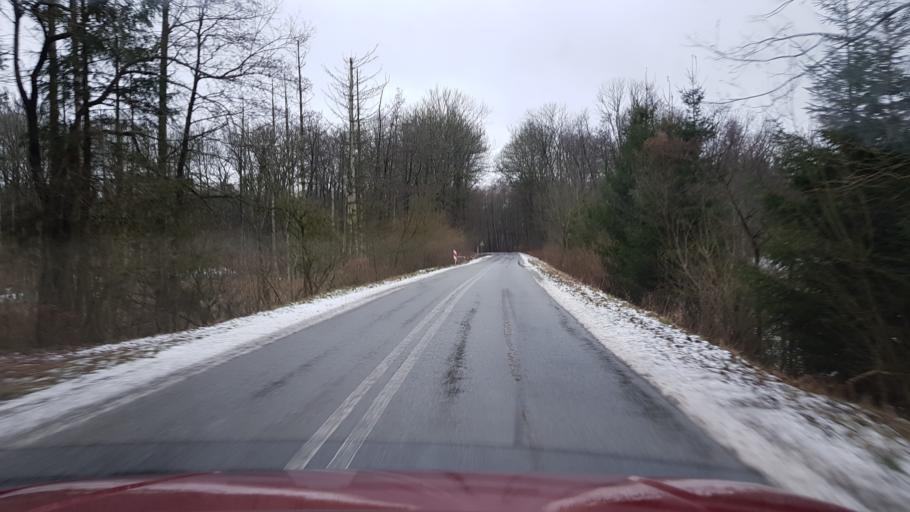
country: PL
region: West Pomeranian Voivodeship
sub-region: Powiat gryficki
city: Ploty
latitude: 53.7166
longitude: 15.2980
